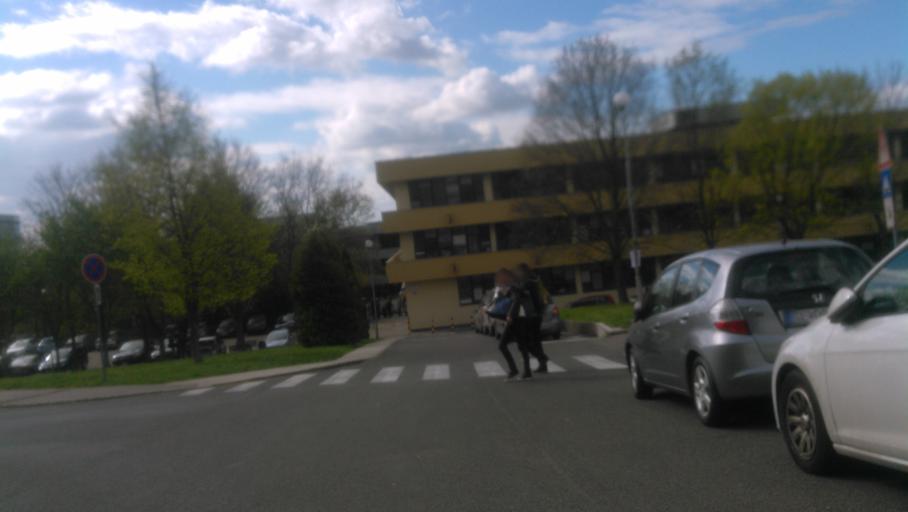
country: SK
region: Bratislavsky
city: Bratislava
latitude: 48.1507
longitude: 17.0718
